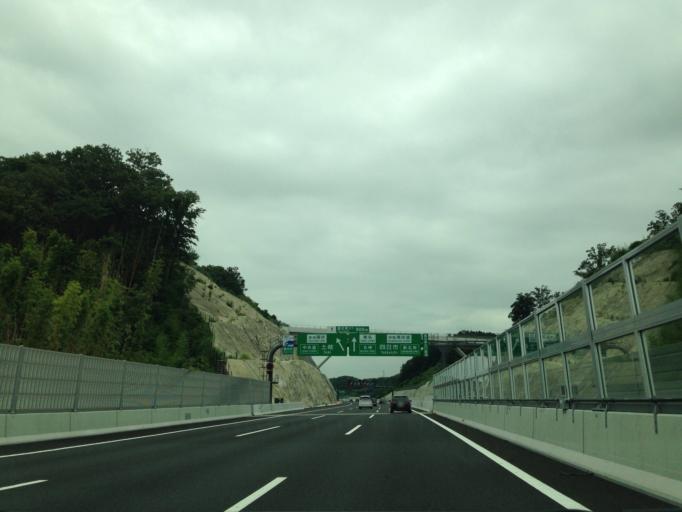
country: JP
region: Aichi
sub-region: Toyota-shi
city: Toyota
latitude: 35.0404
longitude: 137.2102
